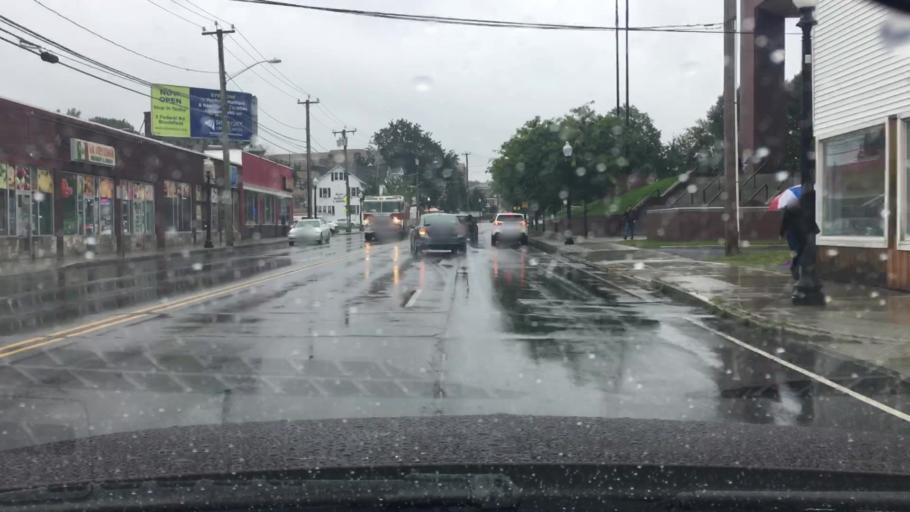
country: US
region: Connecticut
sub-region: Fairfield County
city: Danbury
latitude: 41.3987
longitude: -73.4490
